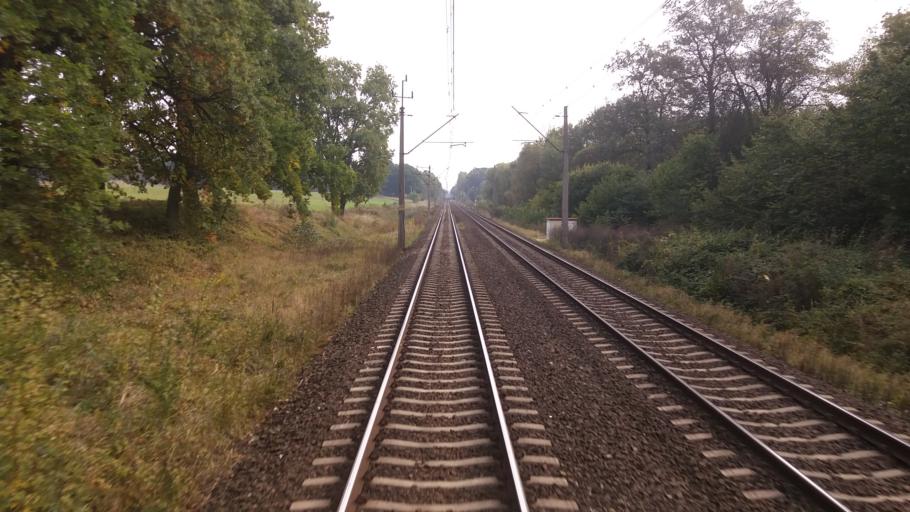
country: PL
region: West Pomeranian Voivodeship
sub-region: Powiat stargardzki
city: Dolice
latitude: 53.1912
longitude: 15.2387
